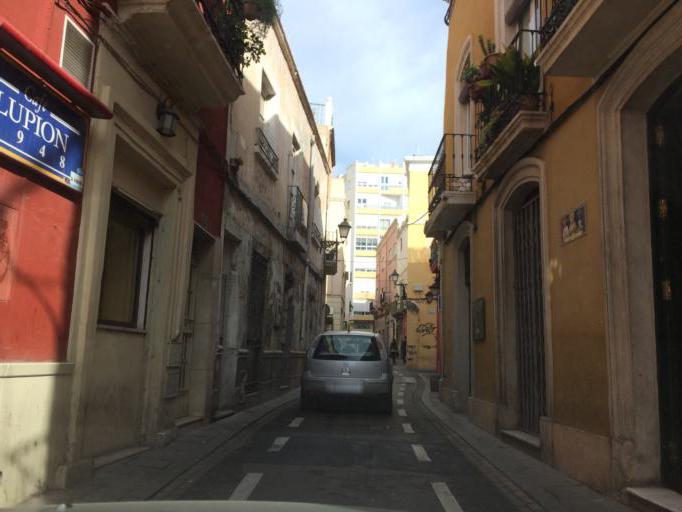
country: ES
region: Andalusia
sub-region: Provincia de Almeria
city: Almeria
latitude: 36.8377
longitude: -2.4657
